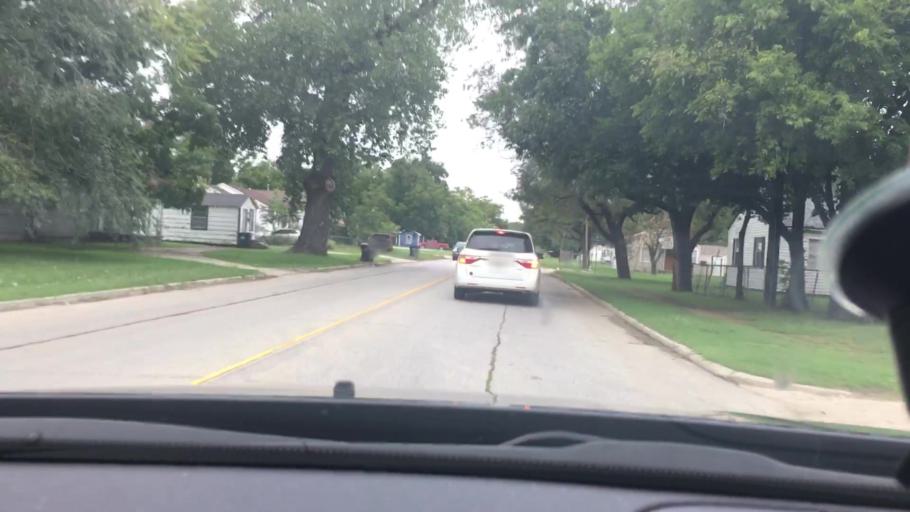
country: US
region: Oklahoma
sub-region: Pontotoc County
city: Ada
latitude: 34.7818
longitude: -96.6806
